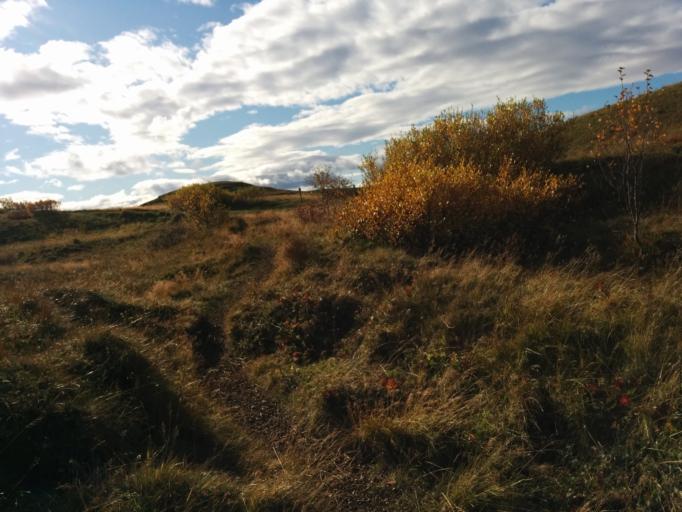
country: IS
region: Northeast
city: Laugar
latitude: 65.5777
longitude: -16.9608
